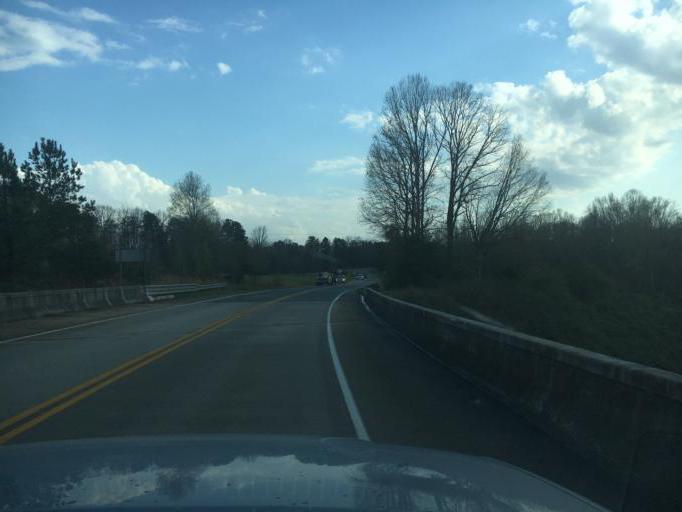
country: US
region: South Carolina
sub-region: Greenville County
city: Parker
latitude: 34.8487
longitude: -82.4940
